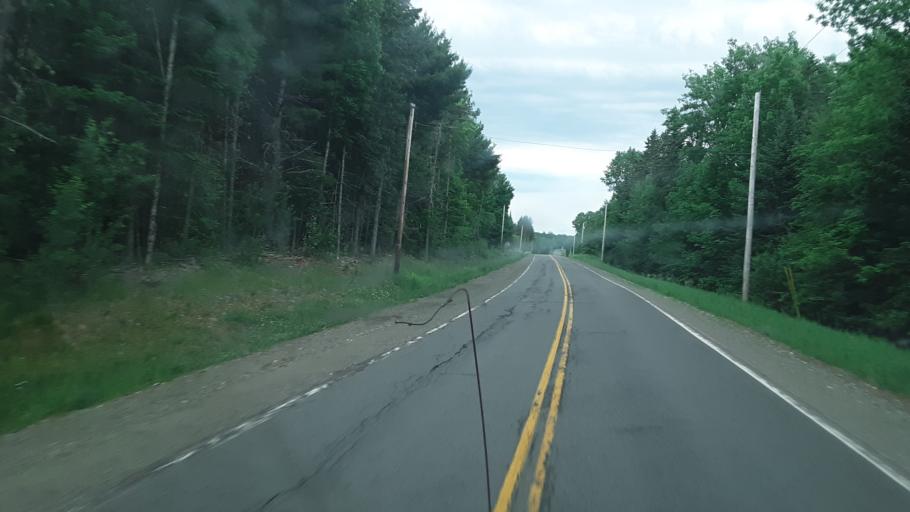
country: US
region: Maine
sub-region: Penobscot County
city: Patten
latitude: 45.7824
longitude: -68.3203
